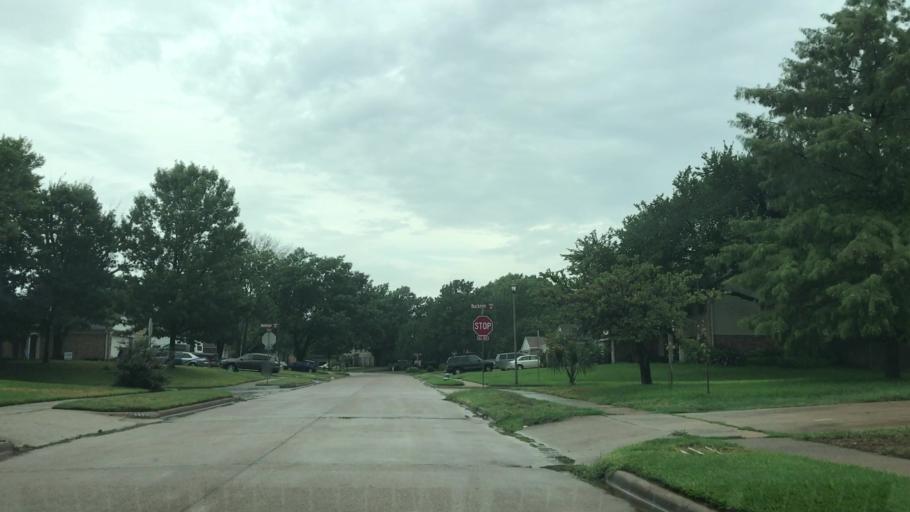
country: US
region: Texas
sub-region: Denton County
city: Flower Mound
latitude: 33.0399
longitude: -97.0577
